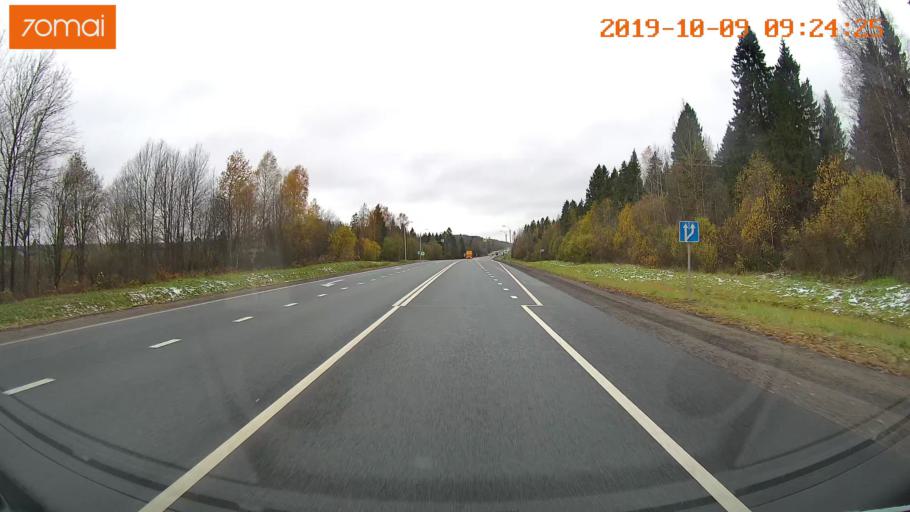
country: RU
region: Vologda
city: Vologda
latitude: 59.0787
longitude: 40.0165
